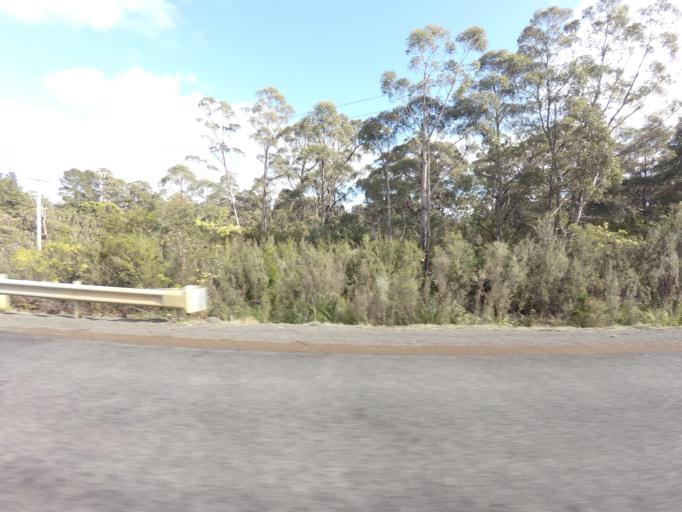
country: AU
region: Tasmania
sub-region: Huon Valley
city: Geeveston
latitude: -43.4206
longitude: 146.9071
